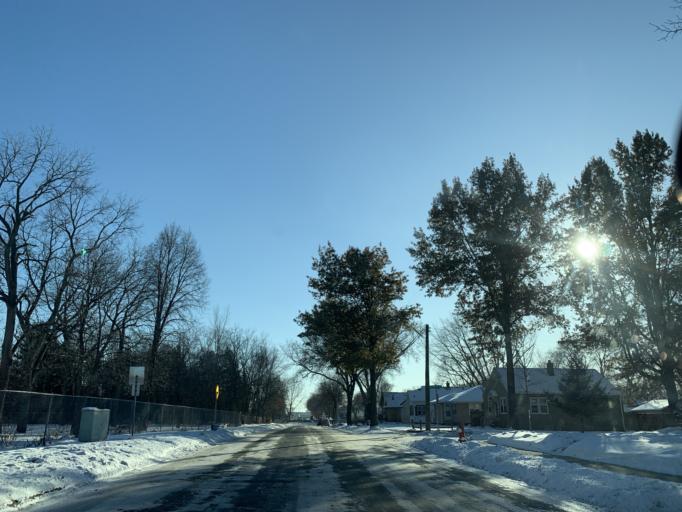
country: US
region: Minnesota
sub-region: Dakota County
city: Mendota Heights
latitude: 44.9003
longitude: -93.2077
